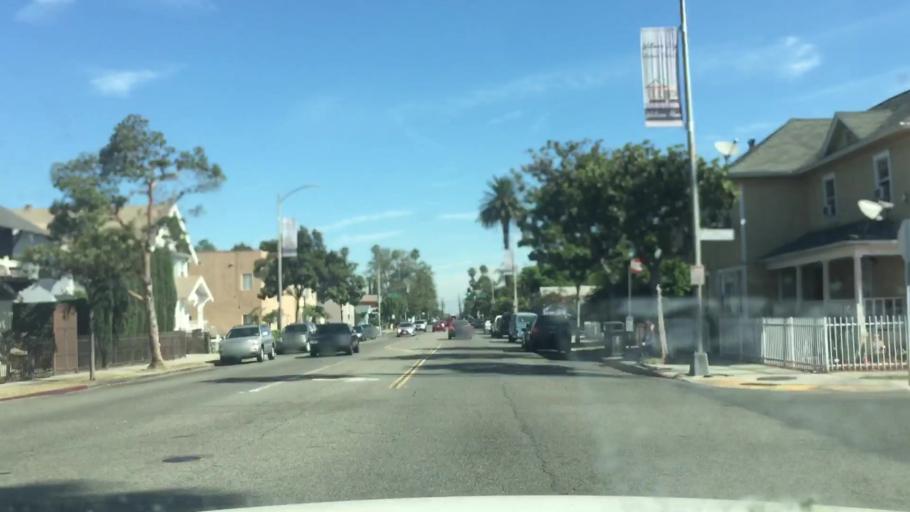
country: US
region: California
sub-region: Los Angeles County
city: Long Beach
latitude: 33.7777
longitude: -118.1980
